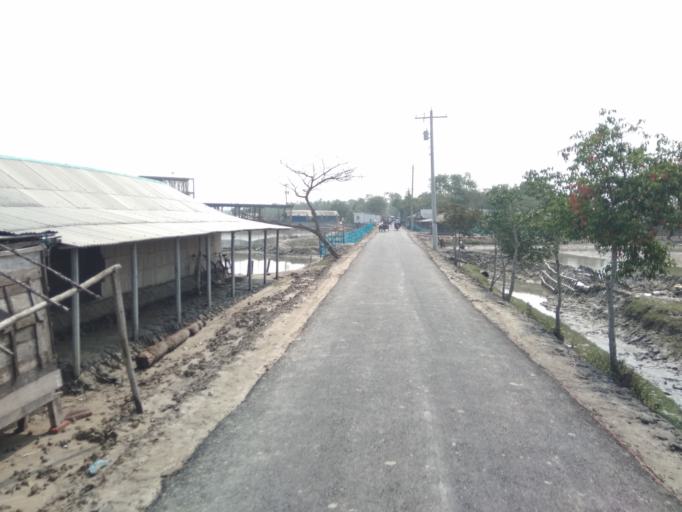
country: IN
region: West Bengal
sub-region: North 24 Parganas
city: Gosaba
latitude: 22.2619
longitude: 89.2235
